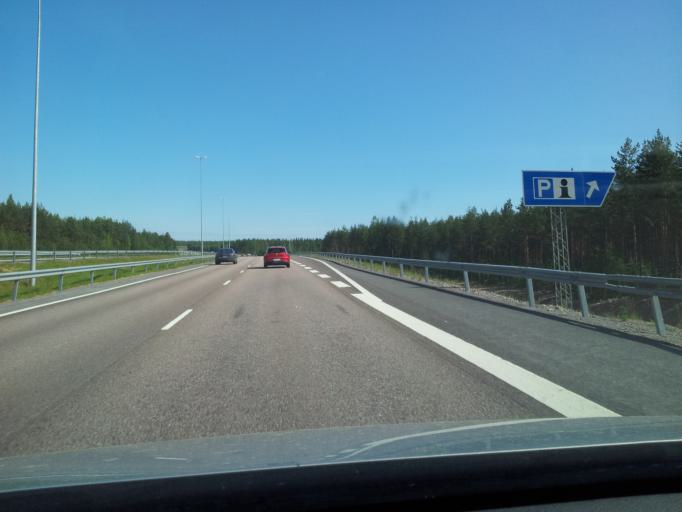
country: FI
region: Uusimaa
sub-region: Loviisa
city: Lovisa
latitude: 60.4666
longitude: 26.1336
